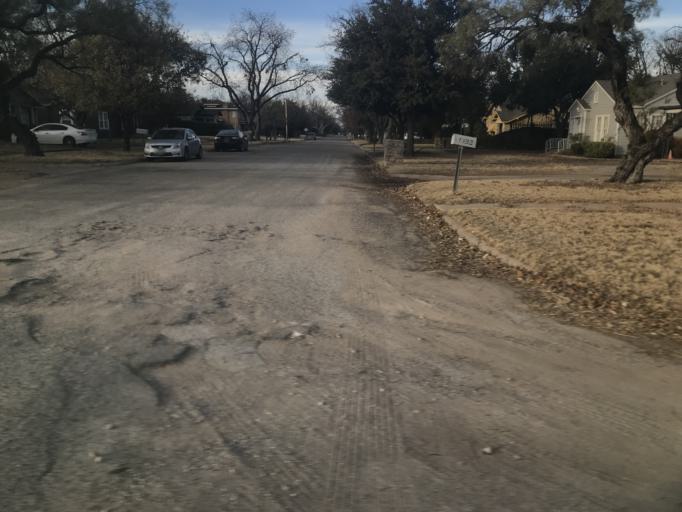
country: US
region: Texas
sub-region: Taylor County
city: Abilene
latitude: 32.4322
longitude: -99.7467
